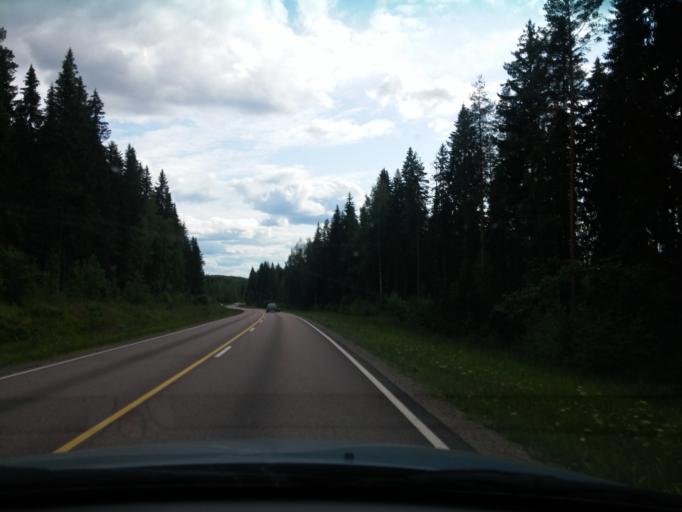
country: FI
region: Central Finland
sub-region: Keuruu
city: Multia
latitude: 62.3719
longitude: 24.7408
